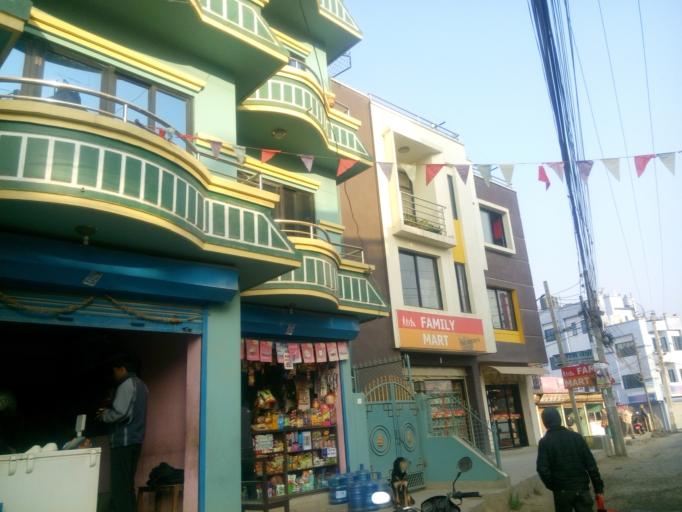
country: NP
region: Central Region
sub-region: Bagmati Zone
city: Patan
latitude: 27.6613
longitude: 85.3366
